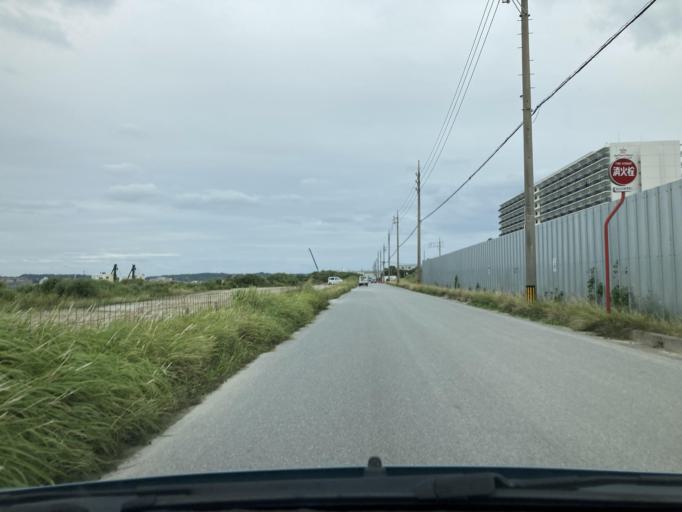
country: JP
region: Okinawa
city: Itoman
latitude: 26.1343
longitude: 127.6531
